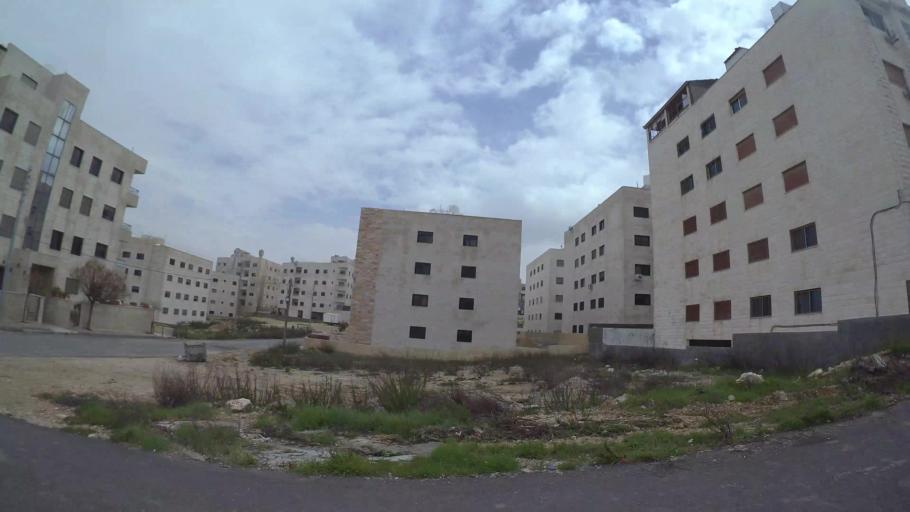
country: JO
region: Amman
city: Umm as Summaq
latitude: 31.9063
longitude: 35.8392
